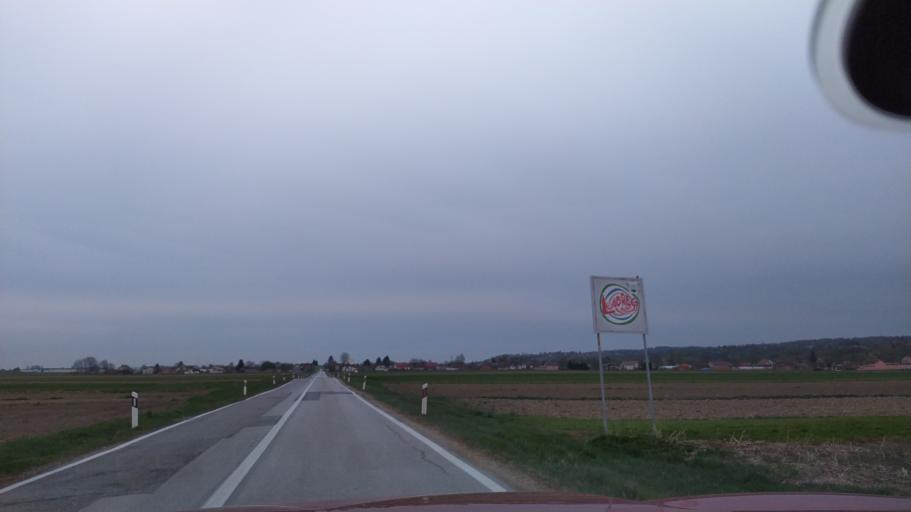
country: HR
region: Varazdinska
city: Ludbreg
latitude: 46.2503
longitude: 16.5748
